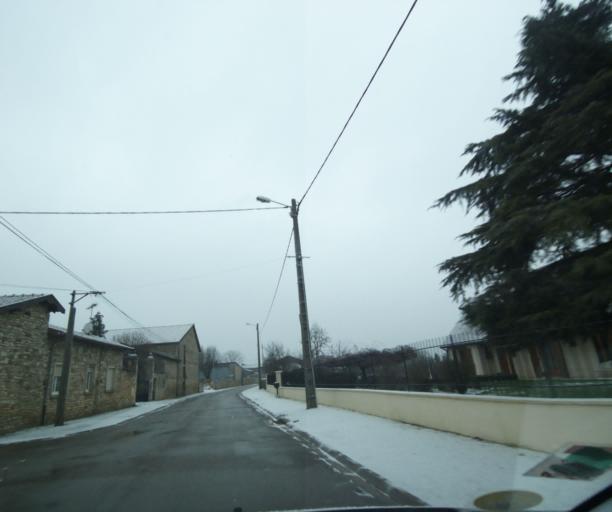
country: FR
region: Champagne-Ardenne
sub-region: Departement de la Haute-Marne
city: Wassy
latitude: 48.4720
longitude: 5.0355
